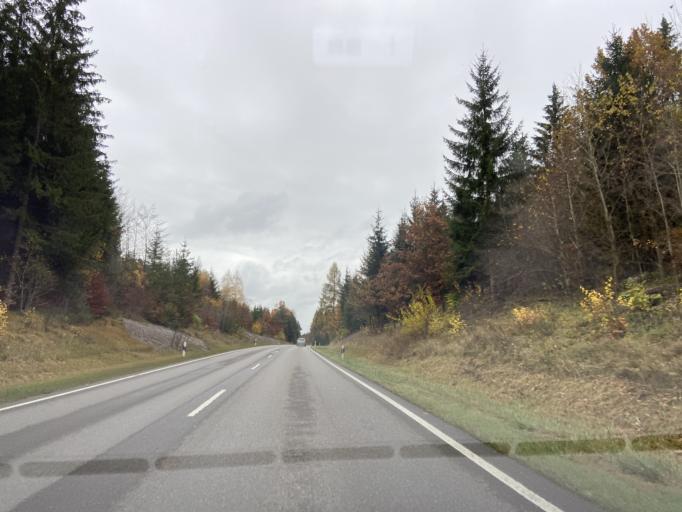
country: DE
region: Baden-Wuerttemberg
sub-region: Tuebingen Region
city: Krauchenwies
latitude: 48.0429
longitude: 9.2393
